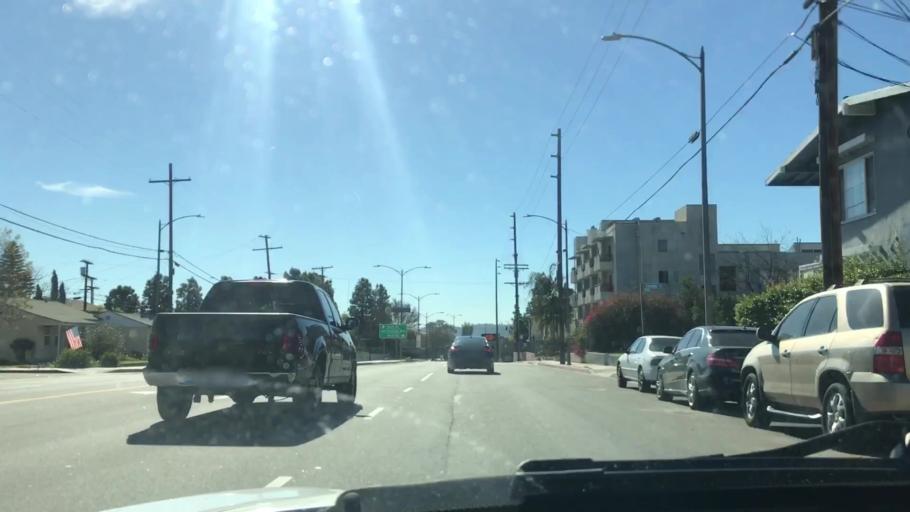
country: US
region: California
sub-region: Los Angeles County
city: North Hollywood
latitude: 34.2079
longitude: -118.3487
